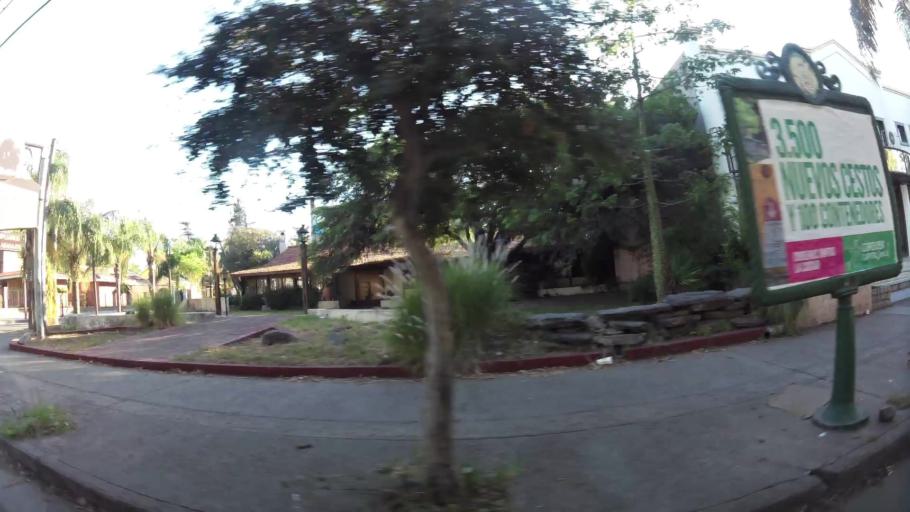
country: AR
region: Cordoba
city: Villa Allende
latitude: -31.3525
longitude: -64.2462
